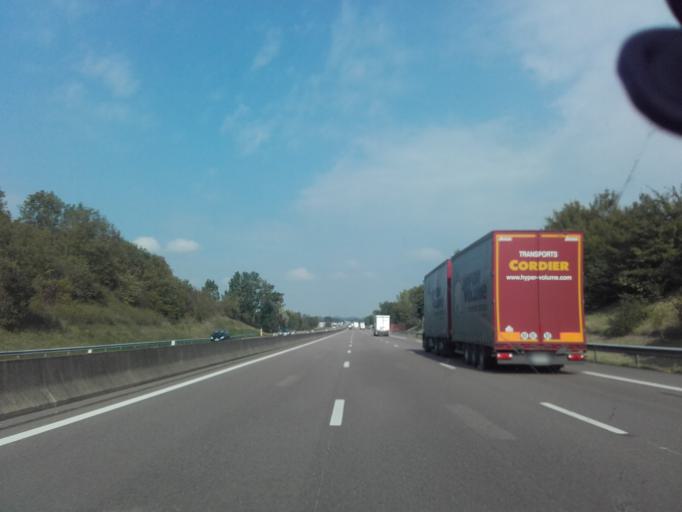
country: FR
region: Rhone-Alpes
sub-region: Departement de l'Ain
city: Pont-de-Vaux
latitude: 46.4708
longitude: 4.8832
